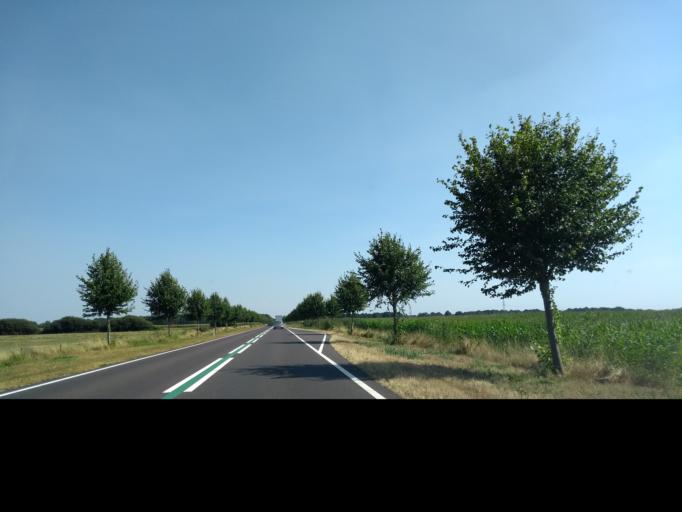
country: NL
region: Overijssel
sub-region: Gemeente Twenterand
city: Vriezenveen
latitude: 52.4023
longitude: 6.6466
